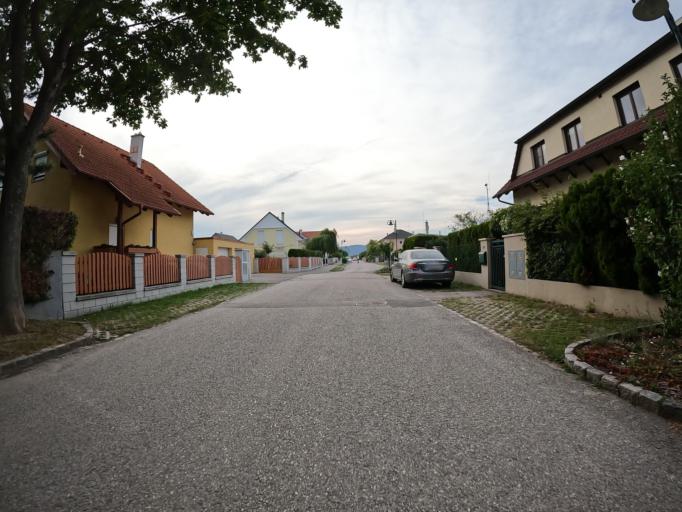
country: AT
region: Lower Austria
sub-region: Politischer Bezirk Baden
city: Trumau
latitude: 47.9979
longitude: 16.3389
